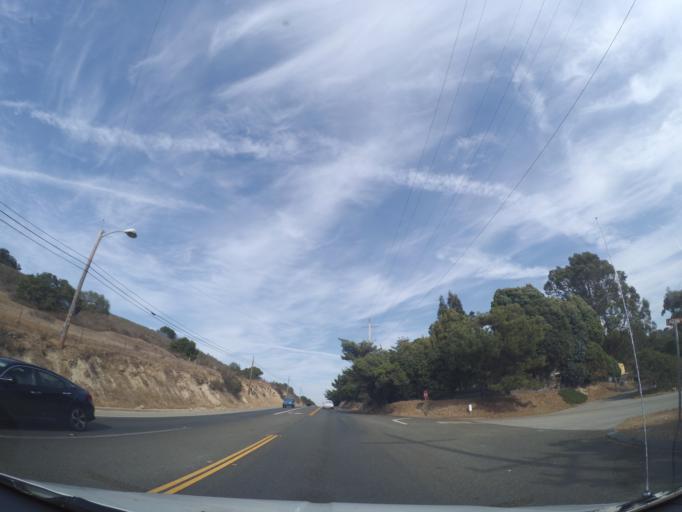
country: US
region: California
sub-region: Monterey County
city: Carmel Valley Village
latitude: 36.5702
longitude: -121.7502
